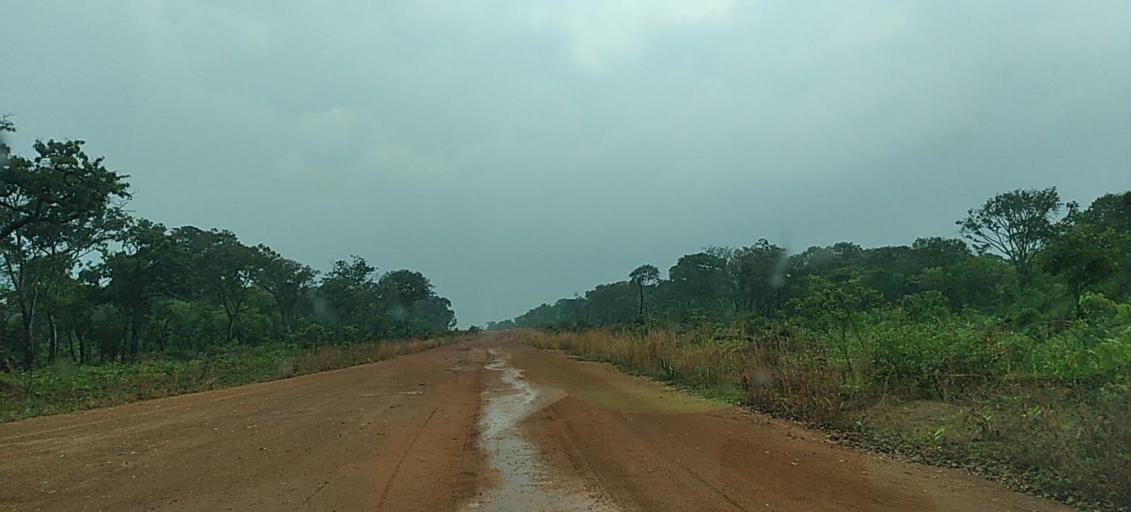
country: ZM
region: North-Western
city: Mwinilunga
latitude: -11.6016
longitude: 24.3939
